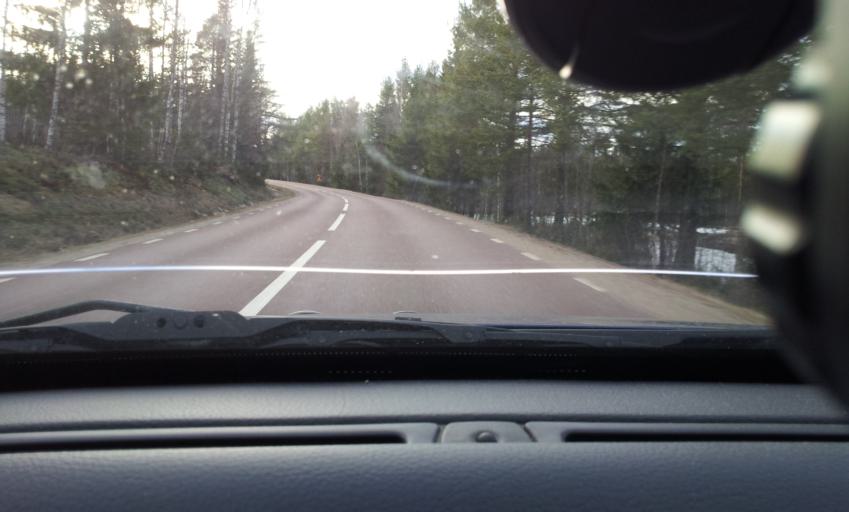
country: SE
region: Jaemtland
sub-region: Harjedalens Kommun
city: Sveg
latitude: 62.1779
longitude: 14.9093
